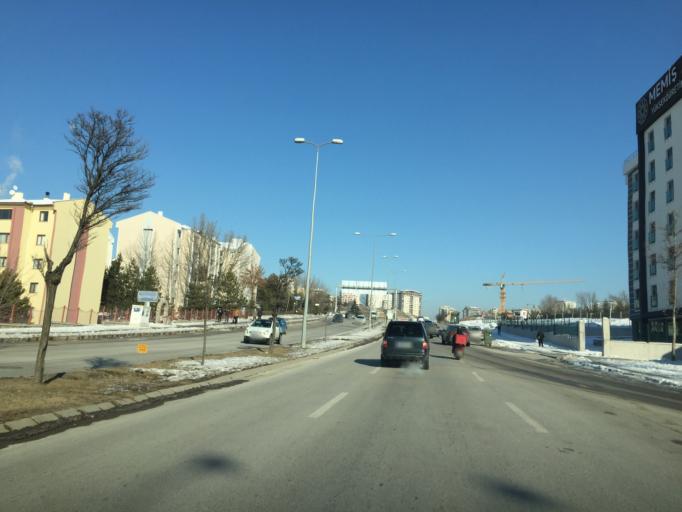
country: TR
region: Ankara
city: Etimesgut
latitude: 39.8841
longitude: 32.6904
